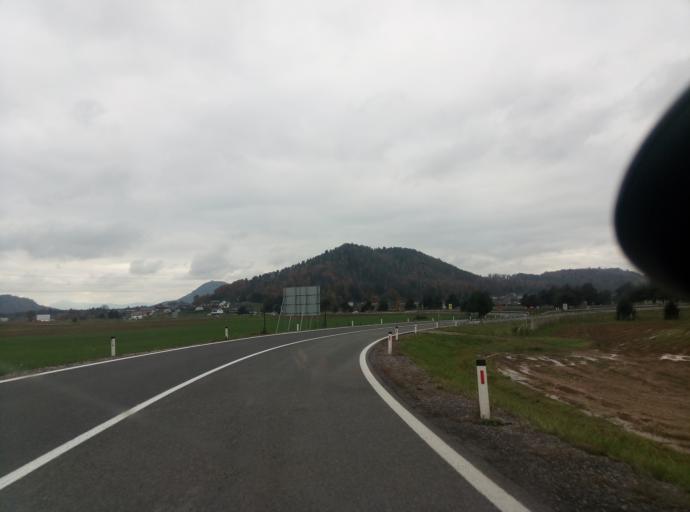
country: SI
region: Vodice
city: Vodice
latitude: 46.1848
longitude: 14.4862
